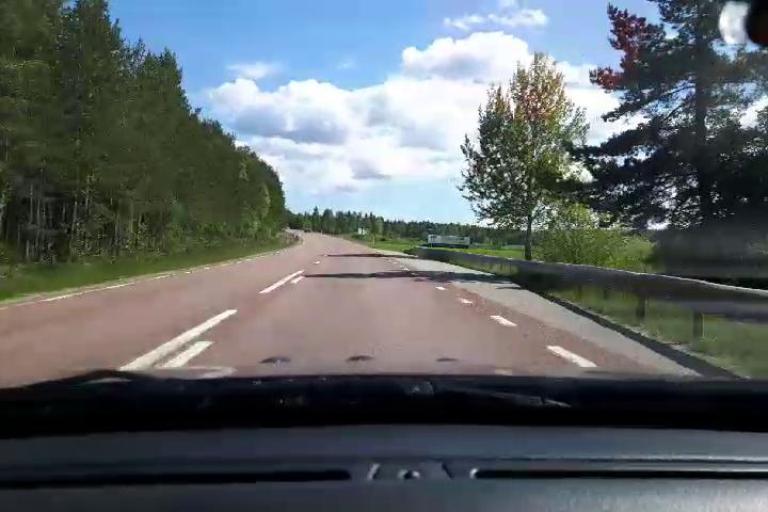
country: SE
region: Gaevleborg
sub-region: Hudiksvalls Kommun
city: Delsbo
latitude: 61.7829
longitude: 16.6362
